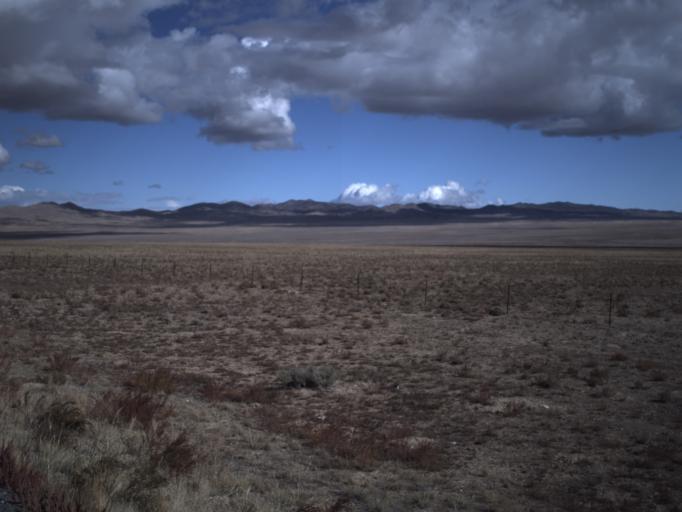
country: US
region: Utah
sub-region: Beaver County
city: Milford
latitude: 38.6697
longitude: -113.8839
